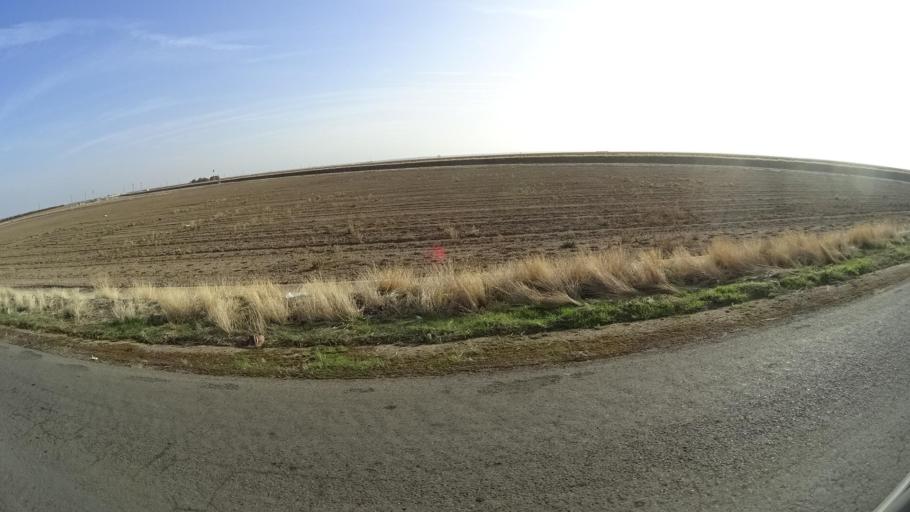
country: US
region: California
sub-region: Kern County
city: McFarland
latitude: 35.7139
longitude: -119.1872
